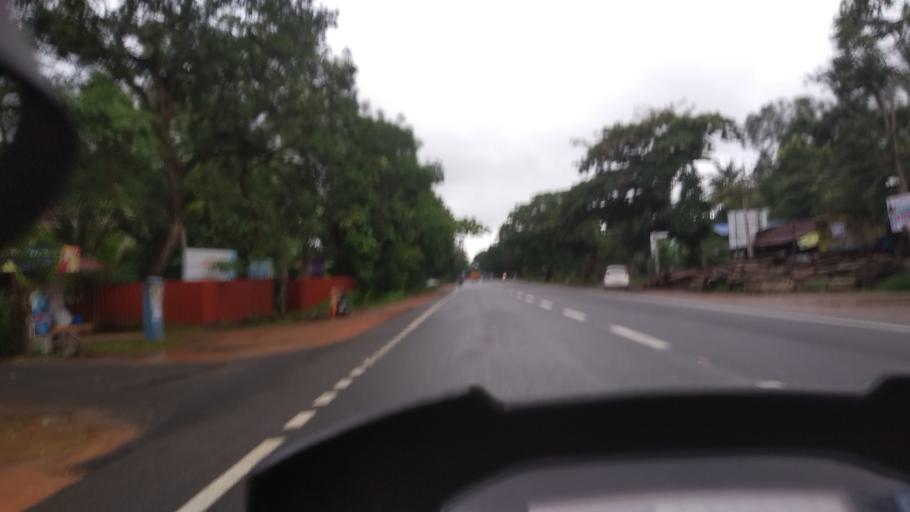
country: IN
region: Kerala
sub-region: Alappuzha
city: Mavelikara
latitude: 9.3106
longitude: 76.4305
